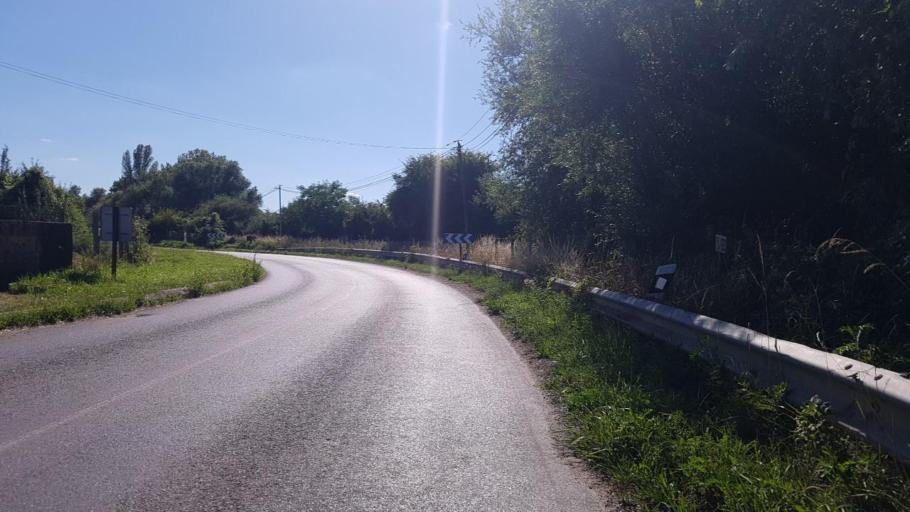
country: FR
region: Ile-de-France
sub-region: Departement de Seine-et-Marne
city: Esbly
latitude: 48.9421
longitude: 2.8003
